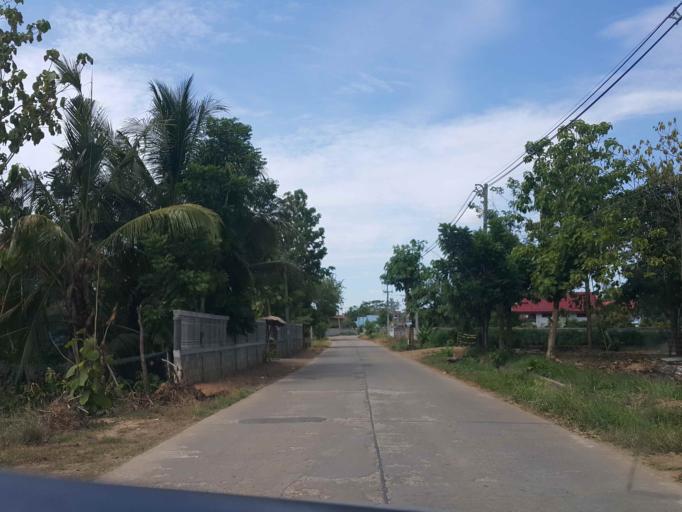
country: TH
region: Sukhothai
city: Thung Saliam
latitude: 17.3332
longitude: 99.5654
